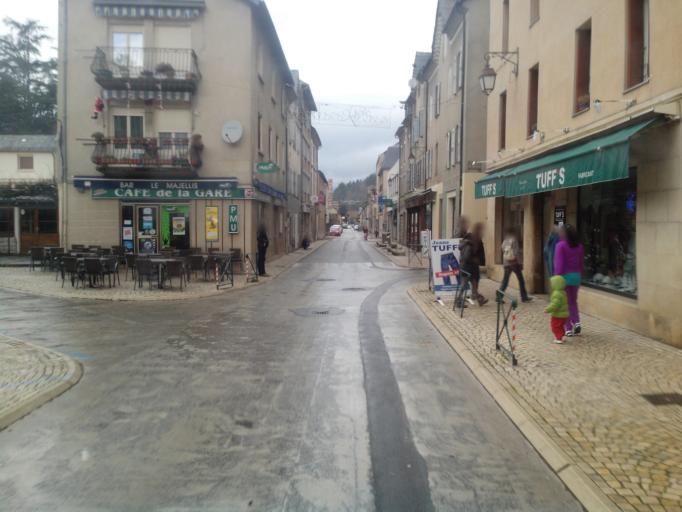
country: FR
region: Languedoc-Roussillon
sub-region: Departement de la Lozere
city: Florac
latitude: 44.3256
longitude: 3.5945
